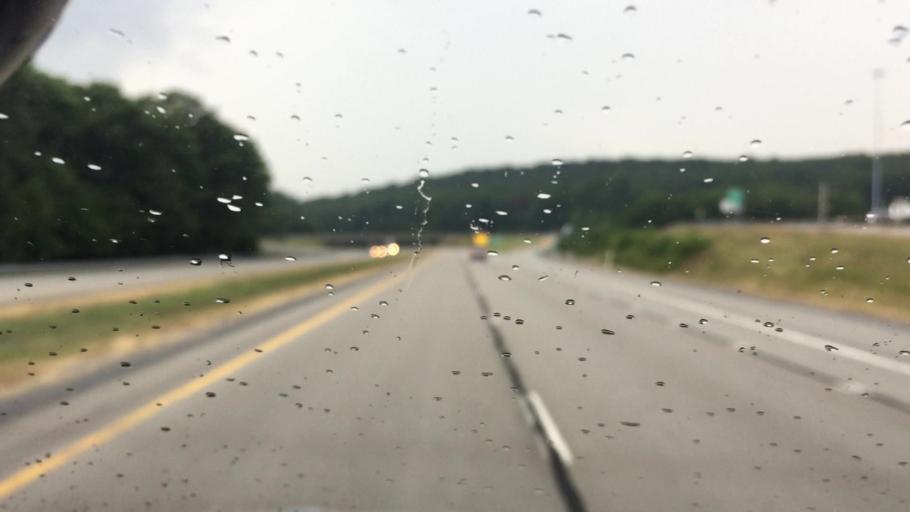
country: US
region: West Virginia
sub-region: Monongalia County
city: Cheat Lake
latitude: 39.6567
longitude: -79.7753
